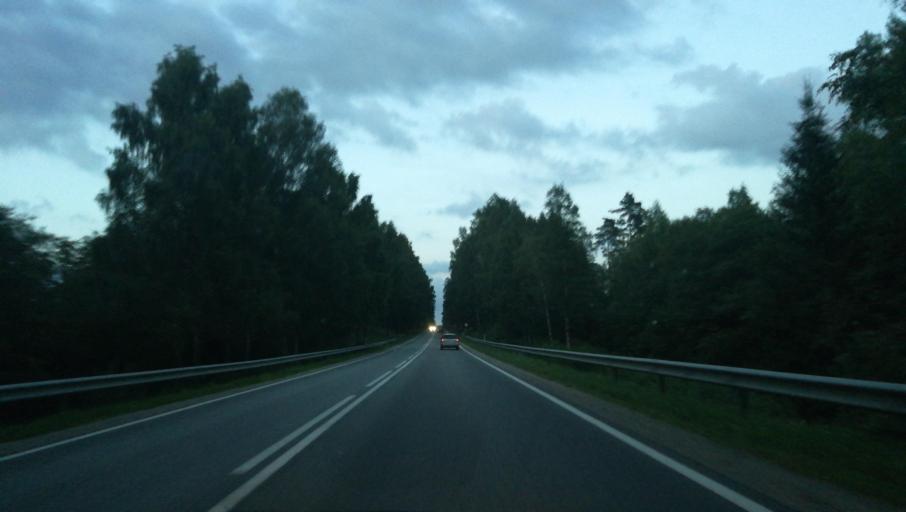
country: LV
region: Amatas Novads
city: Drabesi
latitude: 57.2157
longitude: 25.1905
